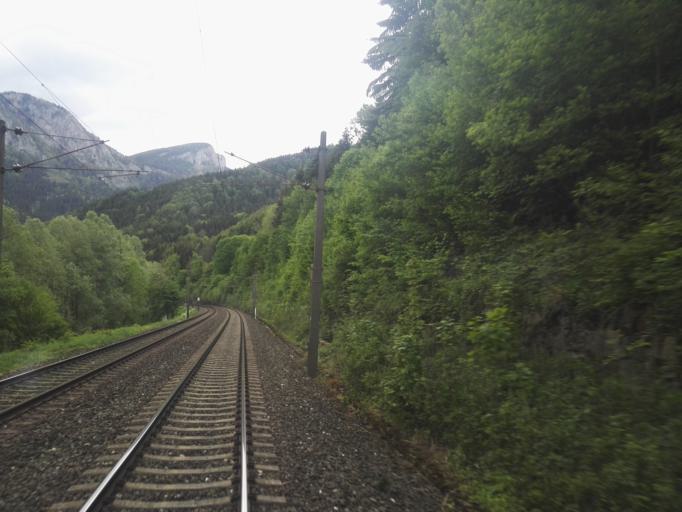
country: AT
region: Styria
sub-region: Politischer Bezirk Graz-Umgebung
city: Rothelstein
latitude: 47.3054
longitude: 15.3757
